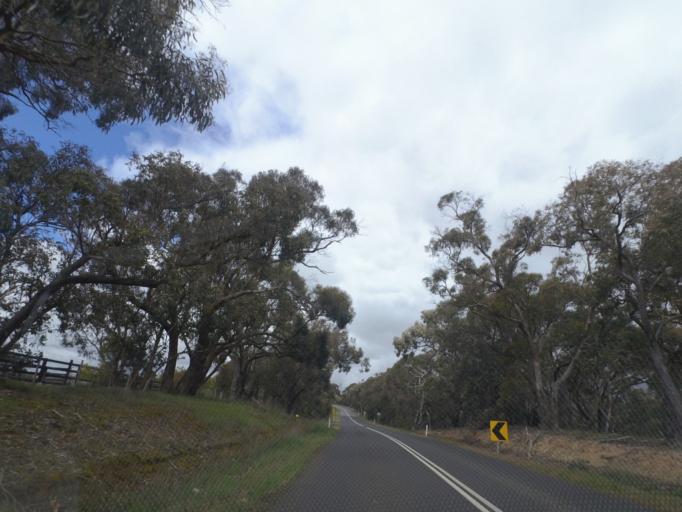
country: AU
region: Victoria
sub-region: Hume
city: Sunbury
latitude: -37.3571
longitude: 144.8046
